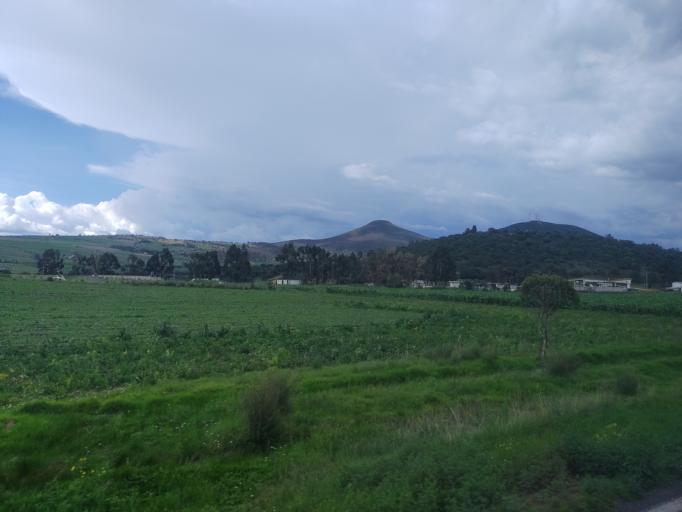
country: MX
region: Mexico
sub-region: Aculco
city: El Colorado
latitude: 20.1027
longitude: -99.7011
